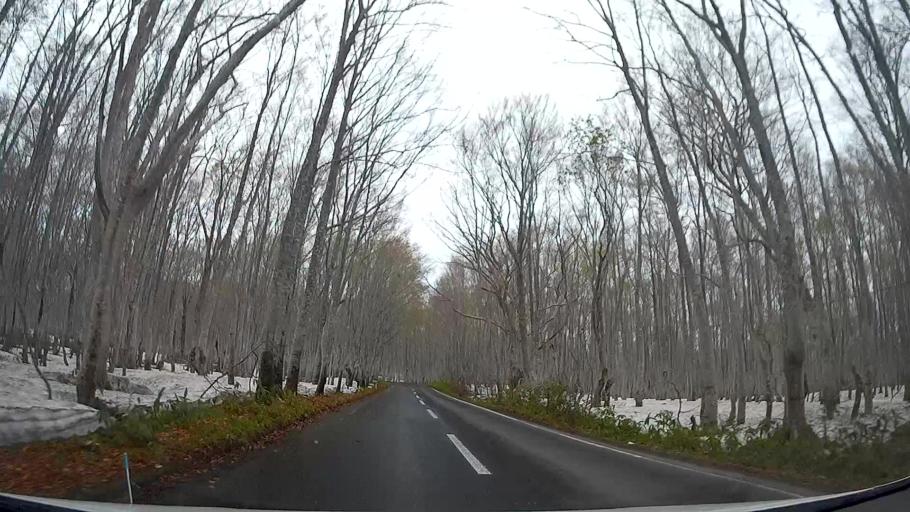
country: JP
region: Aomori
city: Aomori Shi
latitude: 40.6302
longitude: 140.9346
